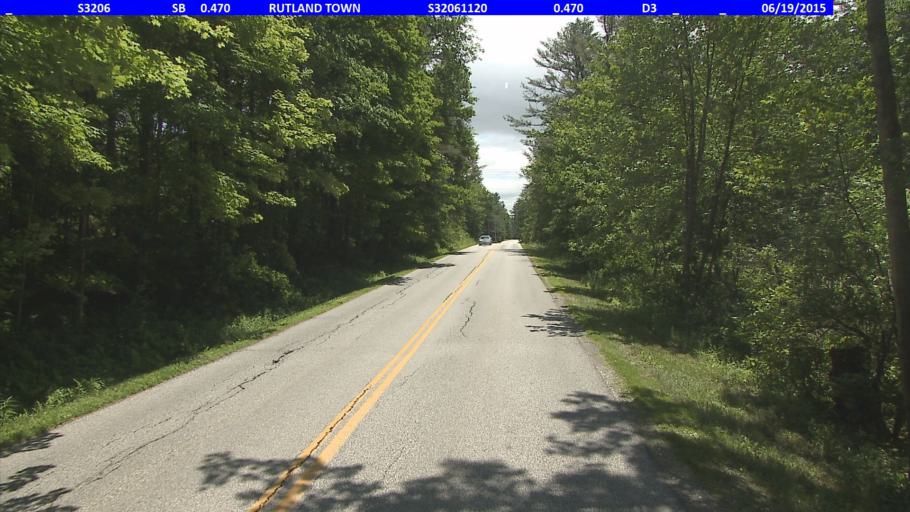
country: US
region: Vermont
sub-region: Rutland County
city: Rutland
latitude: 43.6363
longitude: -72.9905
